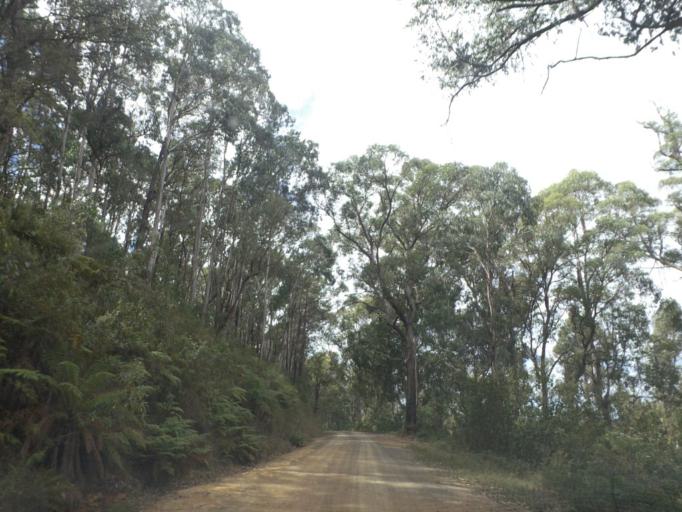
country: AU
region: Victoria
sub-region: Murrindindi
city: Alexandra
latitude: -37.4195
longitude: 145.9710
